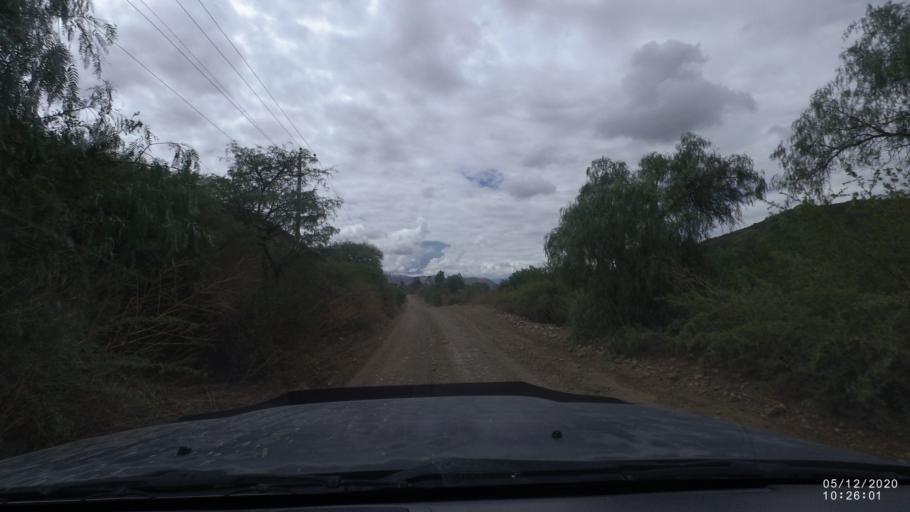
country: BO
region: Cochabamba
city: Sipe Sipe
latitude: -17.5230
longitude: -66.2853
